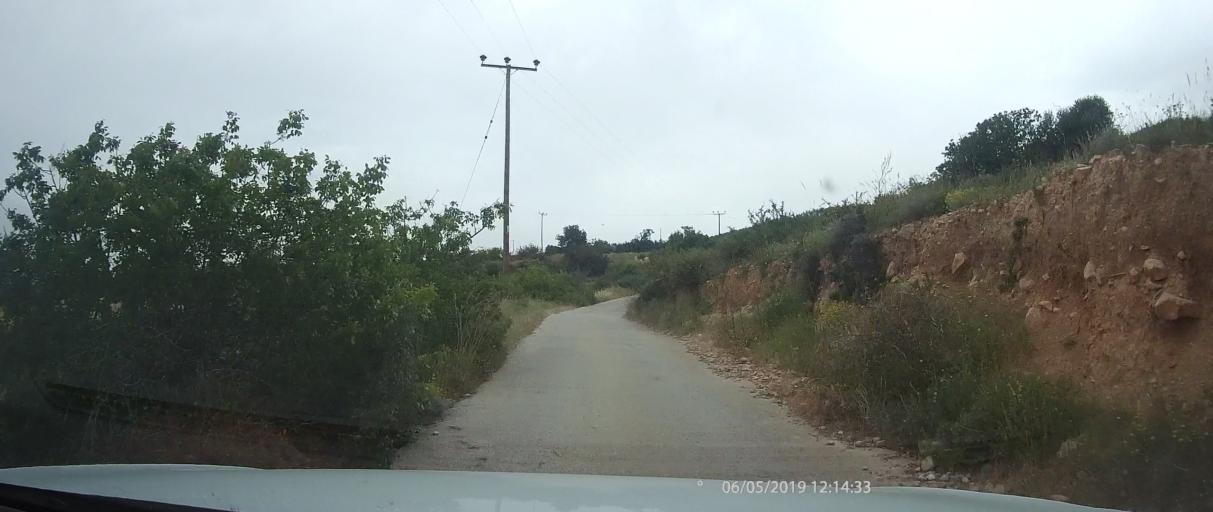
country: CY
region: Pafos
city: Tala
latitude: 34.8471
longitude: 32.4221
